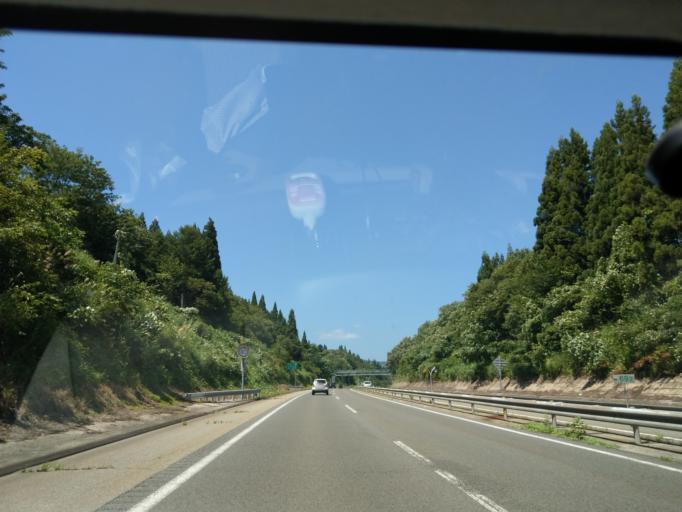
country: JP
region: Akita
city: Omagari
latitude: 39.4113
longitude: 140.4408
